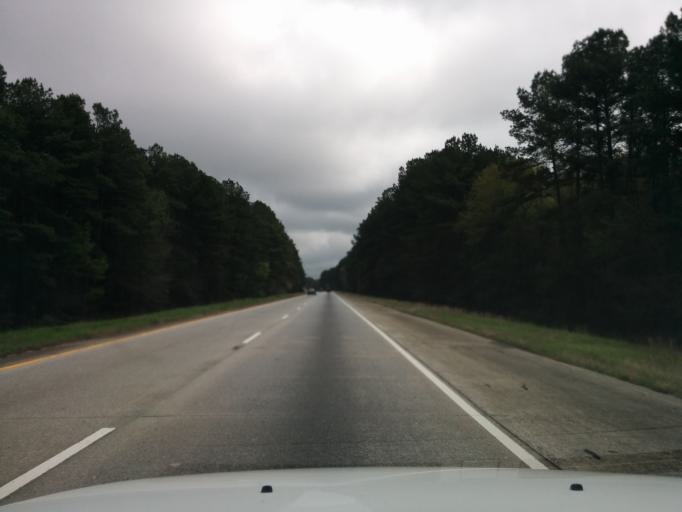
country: US
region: Georgia
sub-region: Toombs County
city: Lyons
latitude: 32.3852
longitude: -82.2553
